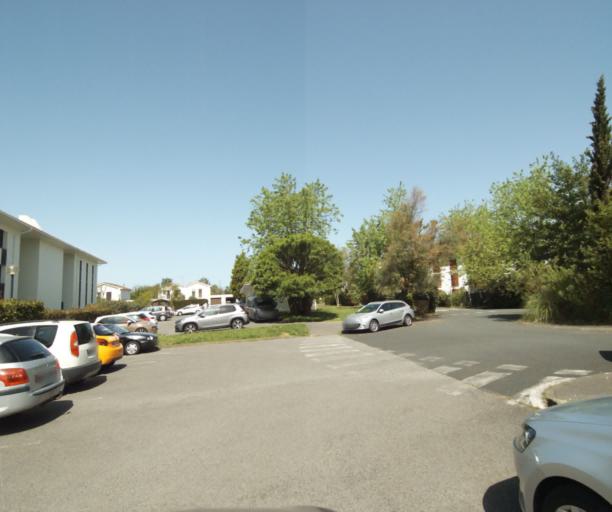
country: FR
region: Aquitaine
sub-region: Departement des Pyrenees-Atlantiques
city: Bayonne
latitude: 43.4754
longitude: -1.4614
